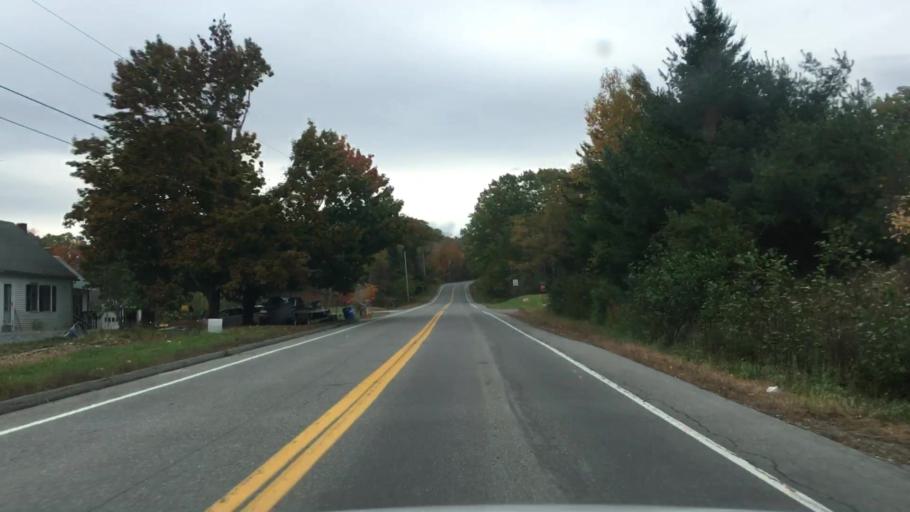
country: US
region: Maine
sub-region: Waldo County
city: Frankfort
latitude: 44.5582
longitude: -68.8518
